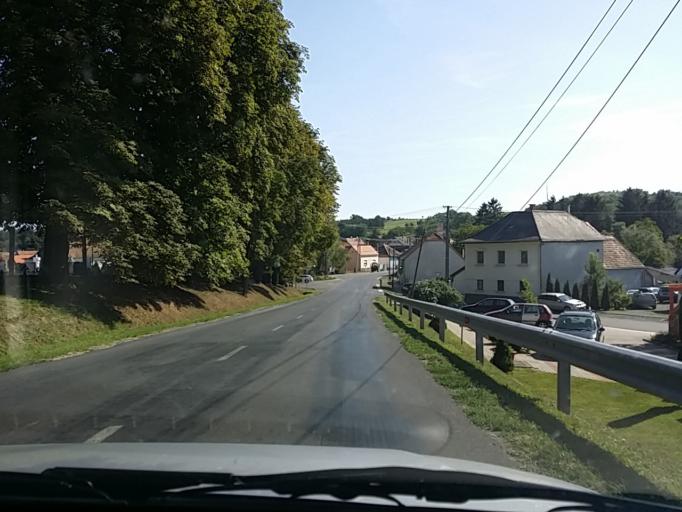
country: AT
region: Burgenland
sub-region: Politischer Bezirk Oberpullendorf
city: Lutzmannsburg
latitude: 47.4269
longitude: 16.6497
